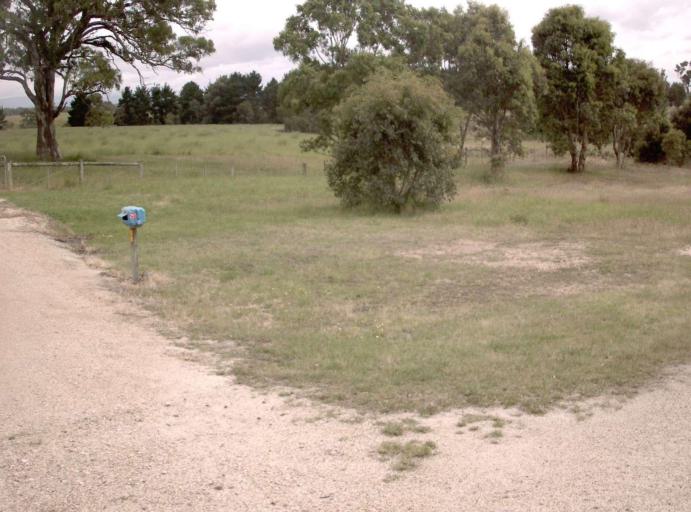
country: AU
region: Victoria
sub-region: Wellington
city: Sale
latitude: -37.9432
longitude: 147.0917
